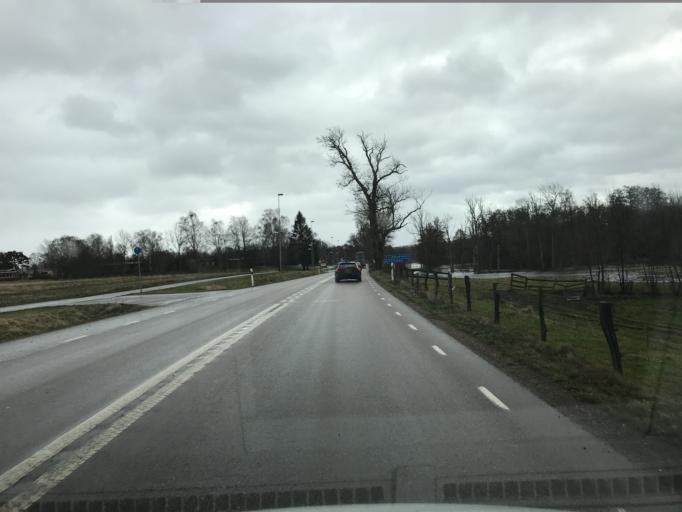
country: SE
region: Skane
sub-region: Klippans Kommun
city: Ljungbyhed
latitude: 56.0849
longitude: 13.2366
